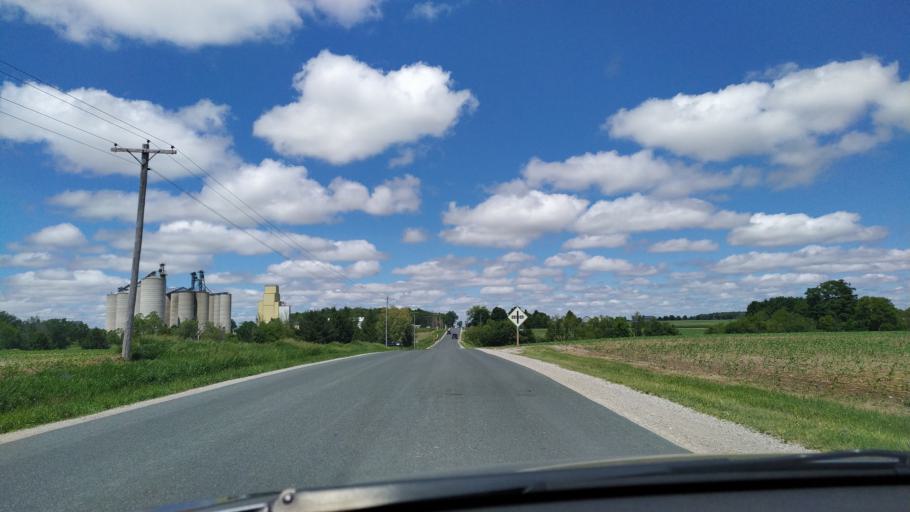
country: CA
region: Ontario
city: Huron East
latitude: 43.4511
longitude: -81.1825
